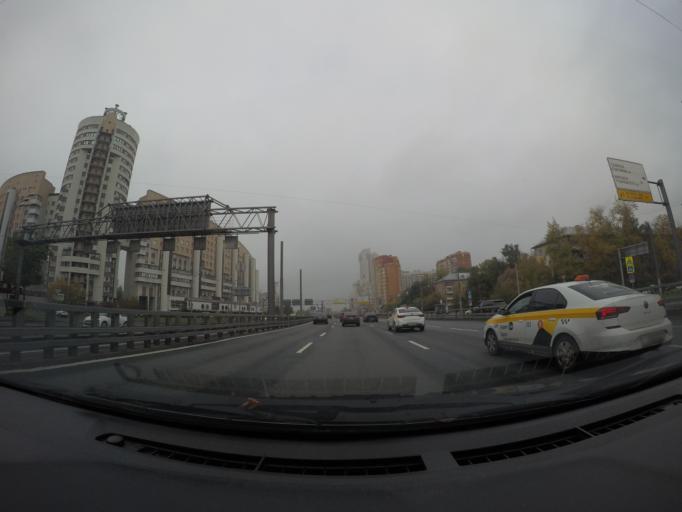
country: RU
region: Moskovskaya
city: Khoroshevo-Mnevniki
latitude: 55.7779
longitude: 37.4606
